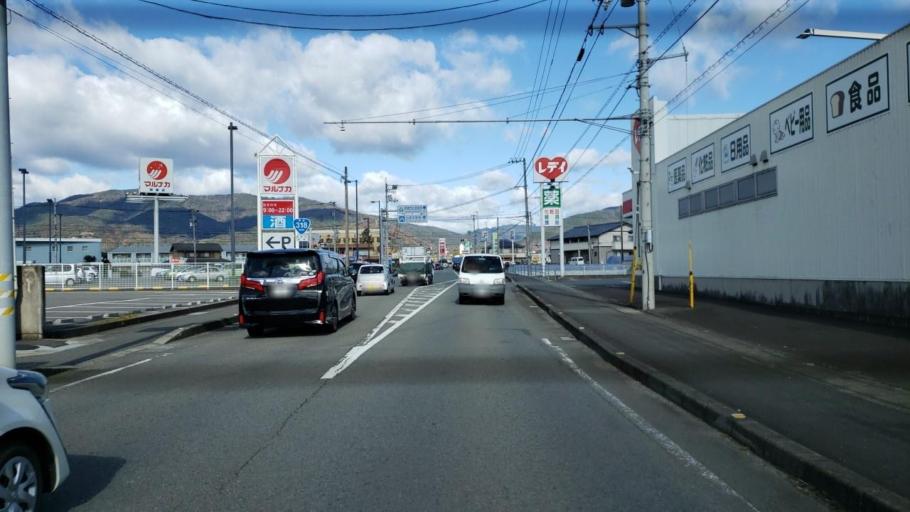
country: JP
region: Tokushima
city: Kamojimacho-jogejima
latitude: 34.1006
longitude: 134.3452
